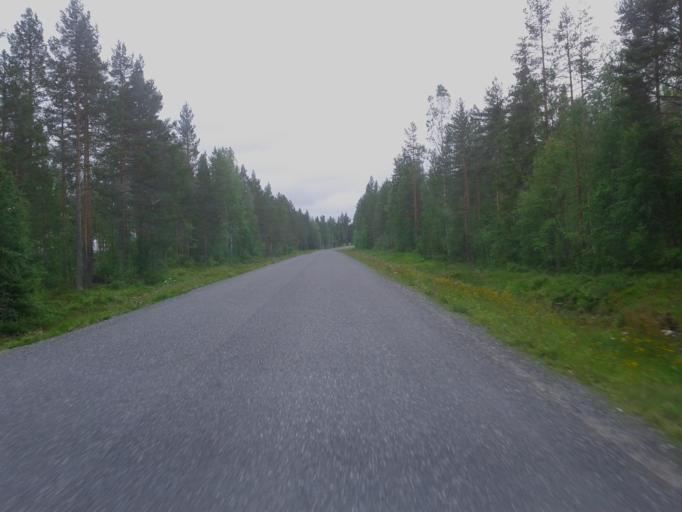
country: SE
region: Vaesterbotten
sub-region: Skelleftea Kommun
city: Storvik
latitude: 65.0101
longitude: 20.7520
